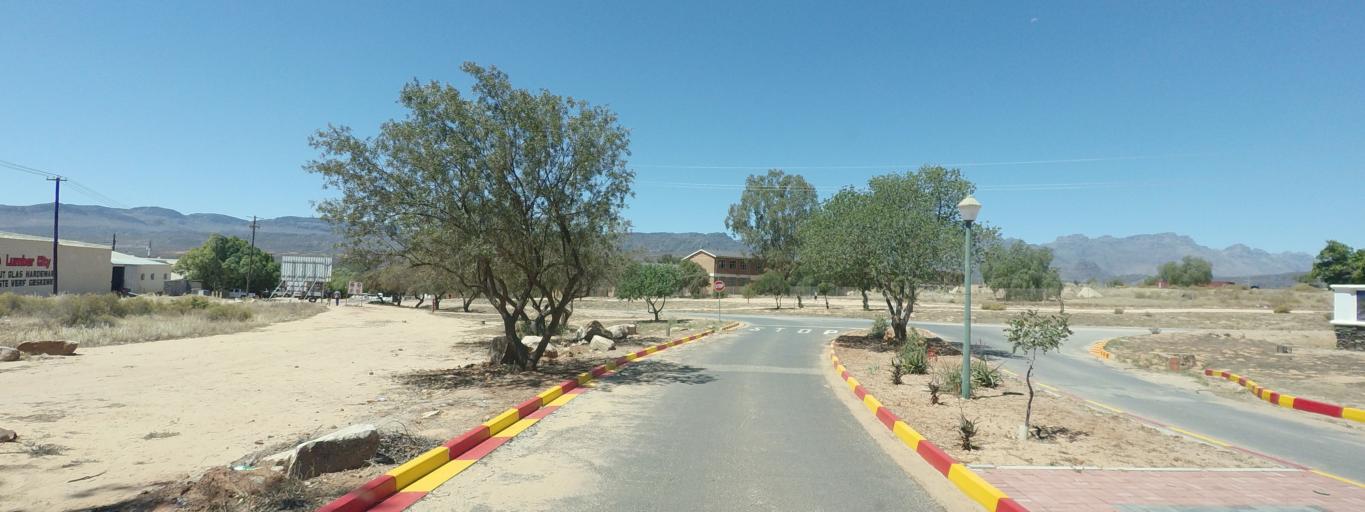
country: ZA
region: Western Cape
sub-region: West Coast District Municipality
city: Clanwilliam
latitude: -32.1898
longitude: 18.8881
